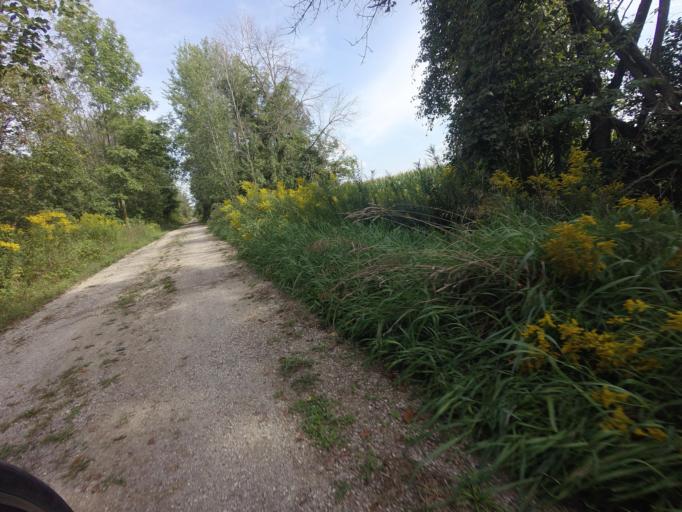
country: CA
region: Ontario
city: Waterloo
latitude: 43.5841
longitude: -80.4171
